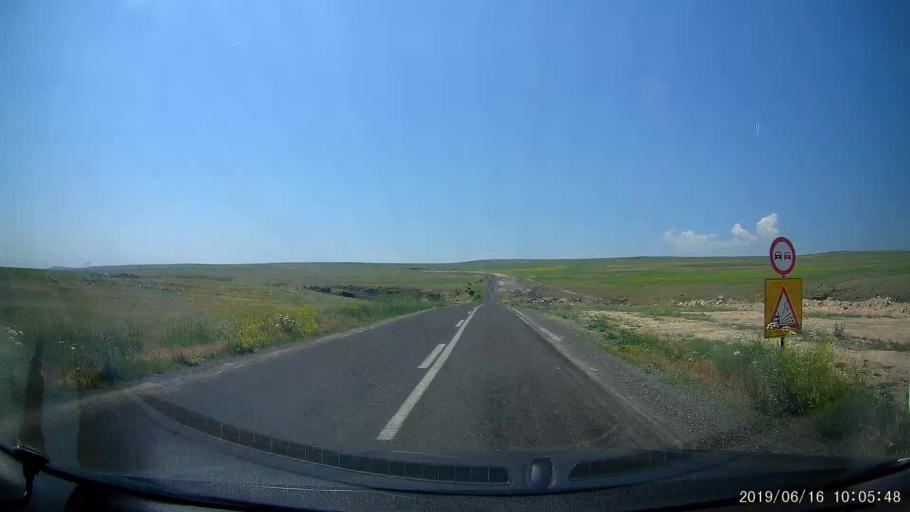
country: TR
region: Kars
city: Digor
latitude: 40.2653
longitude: 43.5398
